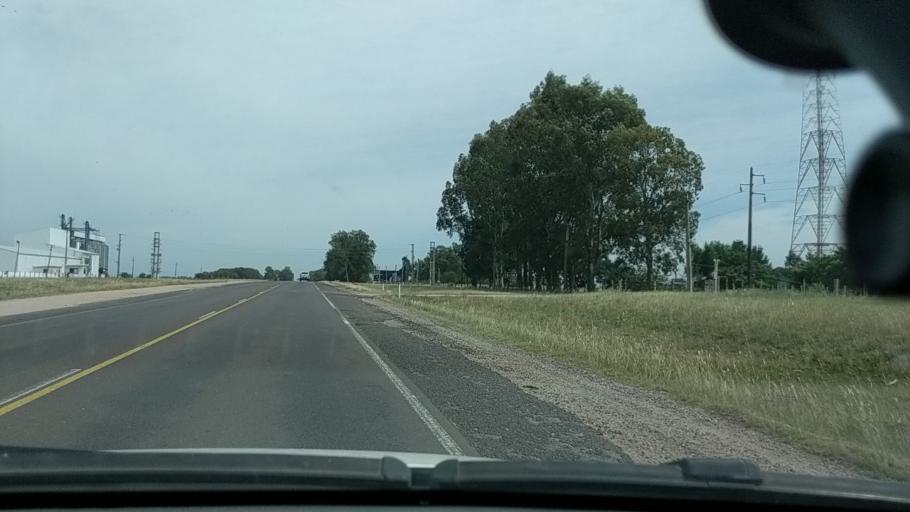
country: UY
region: Durazno
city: Durazno
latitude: -33.4963
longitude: -56.4274
